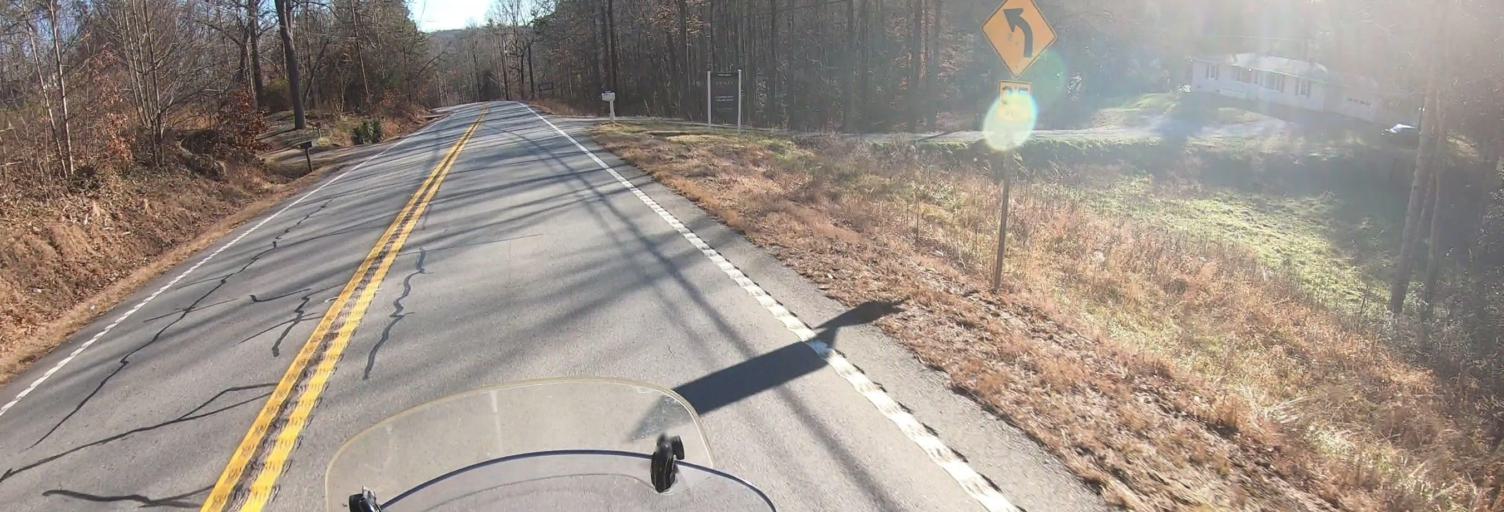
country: US
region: Georgia
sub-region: Fannin County
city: McCaysville
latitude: 34.9672
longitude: -84.3280
